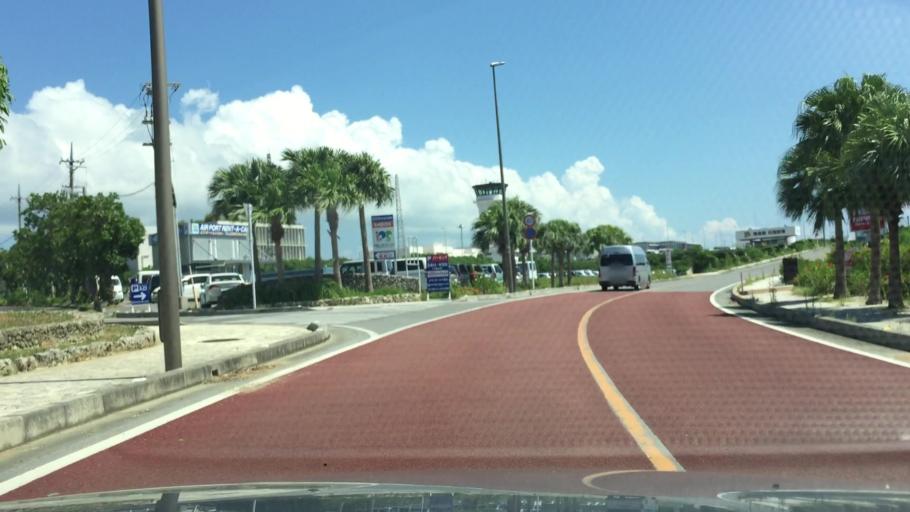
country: JP
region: Okinawa
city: Ishigaki
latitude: 24.3866
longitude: 124.2441
